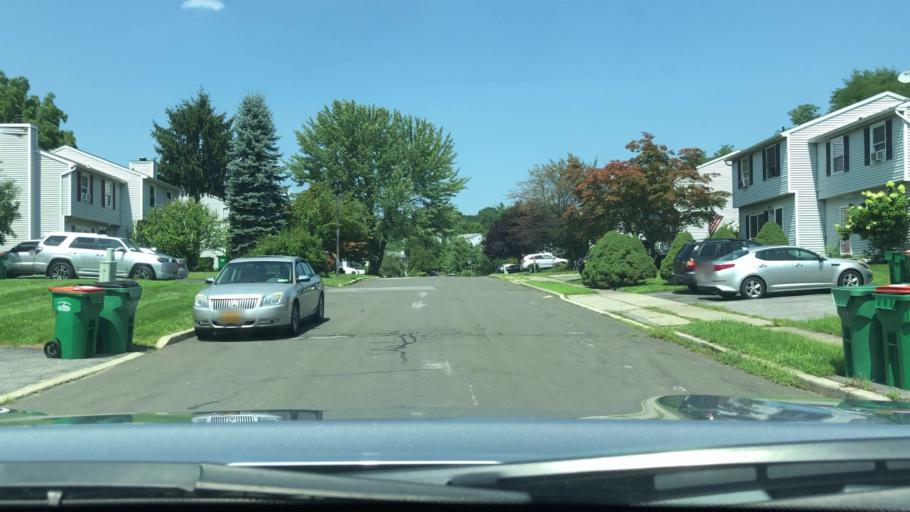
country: US
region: New York
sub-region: Dutchess County
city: Beacon
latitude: 41.4989
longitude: -73.9801
